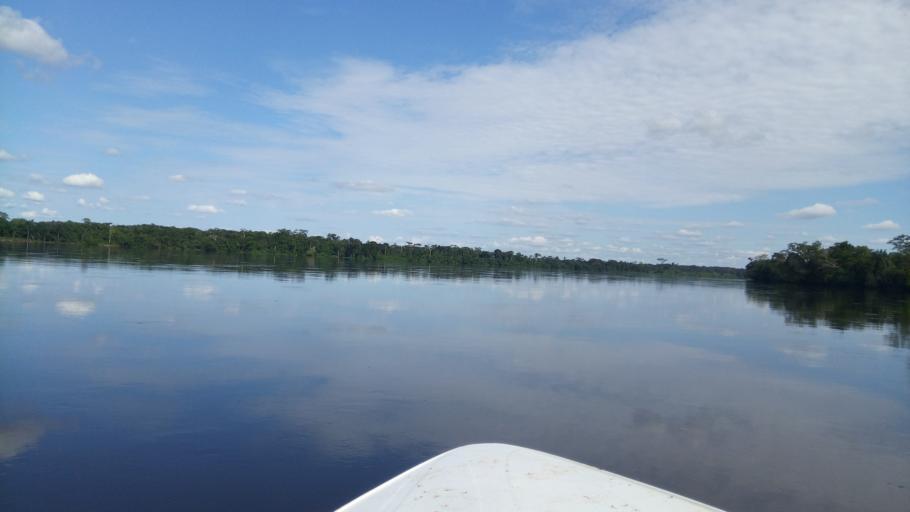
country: CD
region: Eastern Province
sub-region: Sous-Region de la Tshopo
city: Yangambi
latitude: 0.5506
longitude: 24.2448
